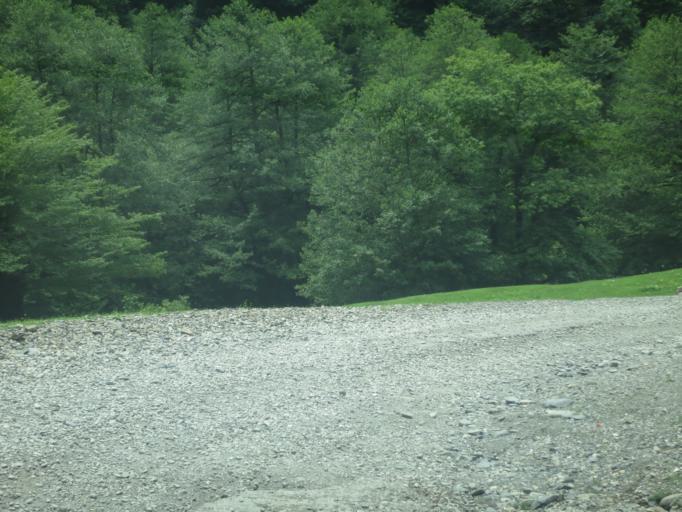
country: GE
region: Kakheti
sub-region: Telavi
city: Telavi
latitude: 42.1939
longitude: 45.4619
